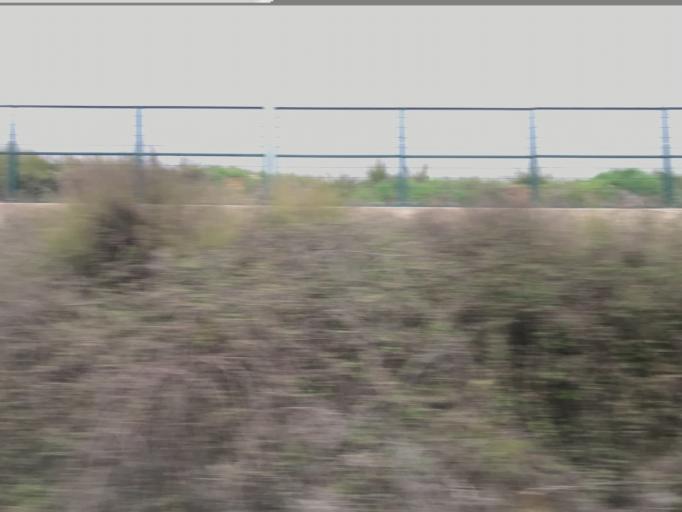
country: TR
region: Istanbul
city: Pendik
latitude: 40.8652
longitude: 29.2679
